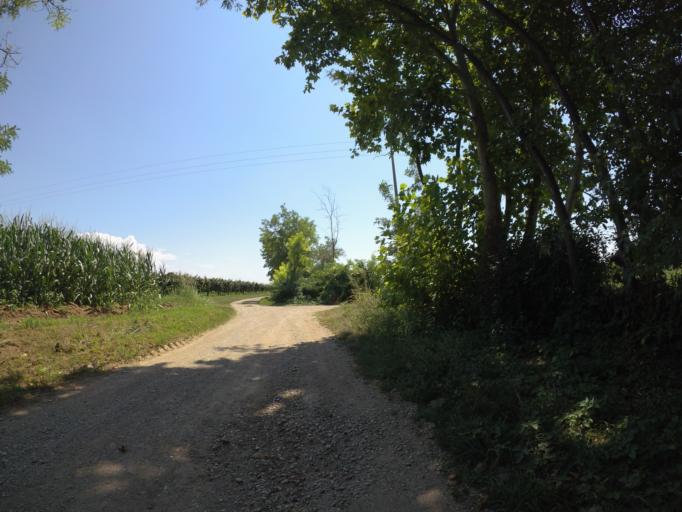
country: IT
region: Friuli Venezia Giulia
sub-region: Provincia di Udine
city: Castions di Strada
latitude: 45.9297
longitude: 13.1867
